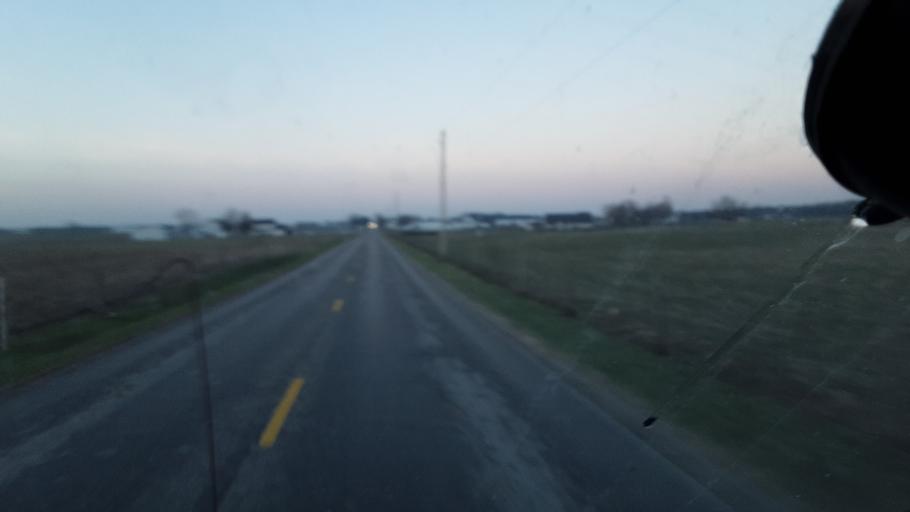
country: US
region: Indiana
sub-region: Allen County
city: Grabill
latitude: 41.2266
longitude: -84.9424
